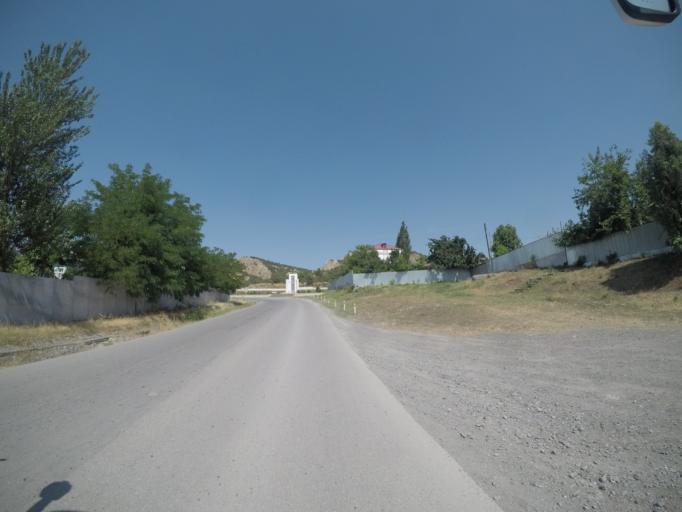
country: AZ
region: Agdas
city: Agdas
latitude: 40.7120
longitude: 47.5479
